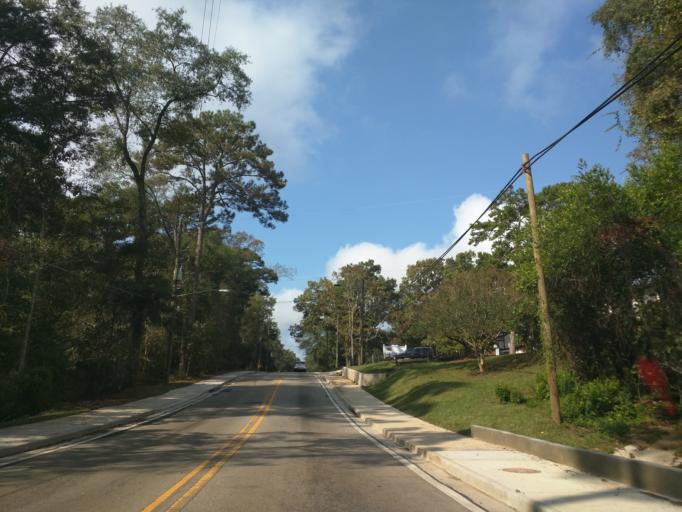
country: US
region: Florida
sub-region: Leon County
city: Tallahassee
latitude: 30.4675
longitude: -84.2743
